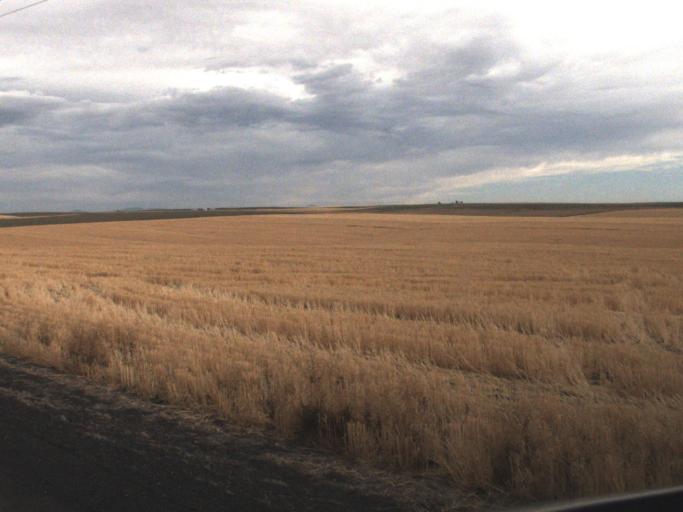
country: US
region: Washington
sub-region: Okanogan County
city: Coulee Dam
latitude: 47.6021
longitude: -118.7861
